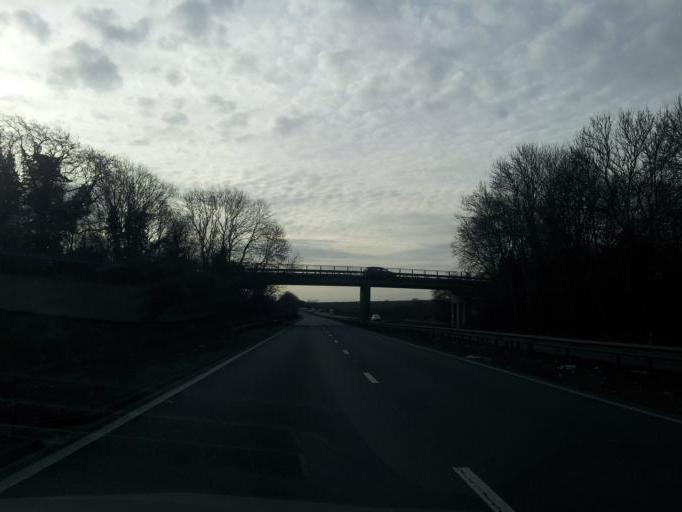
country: GB
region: England
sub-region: District of Rutland
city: Tickencote
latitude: 52.6695
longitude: -0.5267
